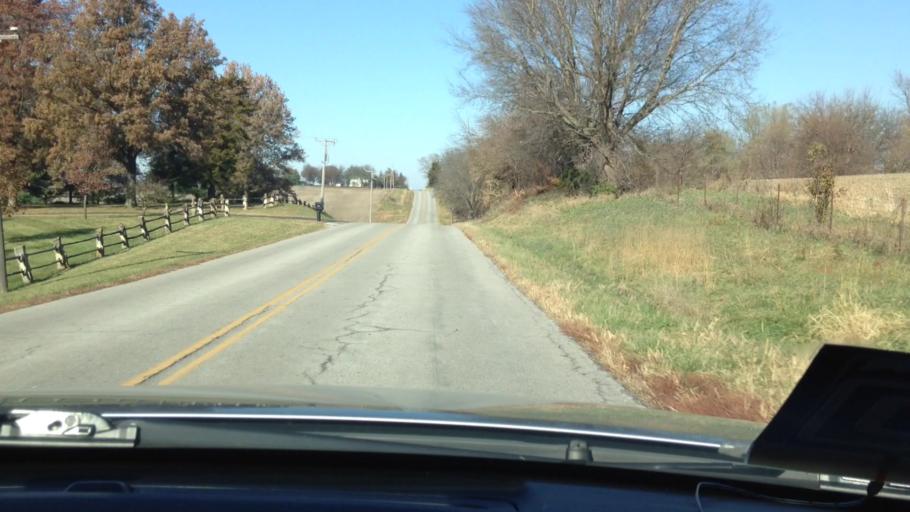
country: US
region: Missouri
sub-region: Platte County
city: Weston
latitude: 39.4350
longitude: -94.8541
